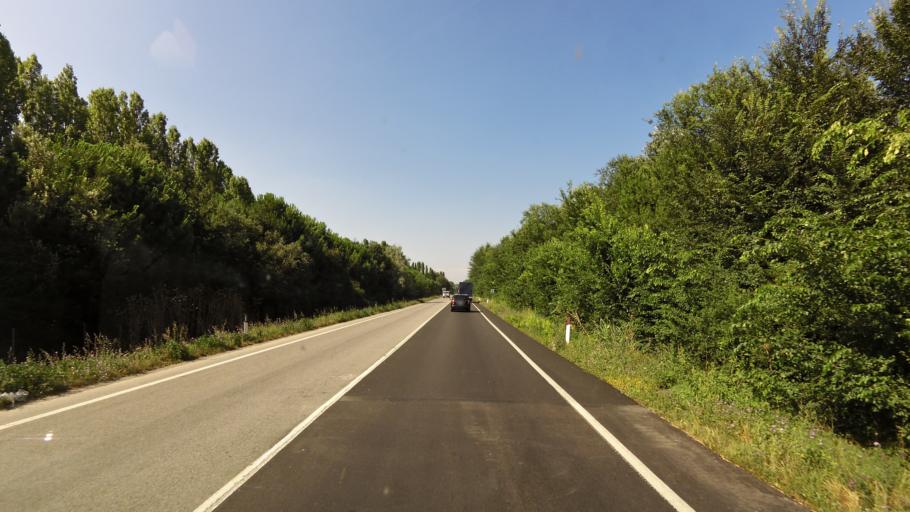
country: IT
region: Emilia-Romagna
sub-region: Provincia di Ravenna
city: Ravenna
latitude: 44.4738
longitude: 12.2096
